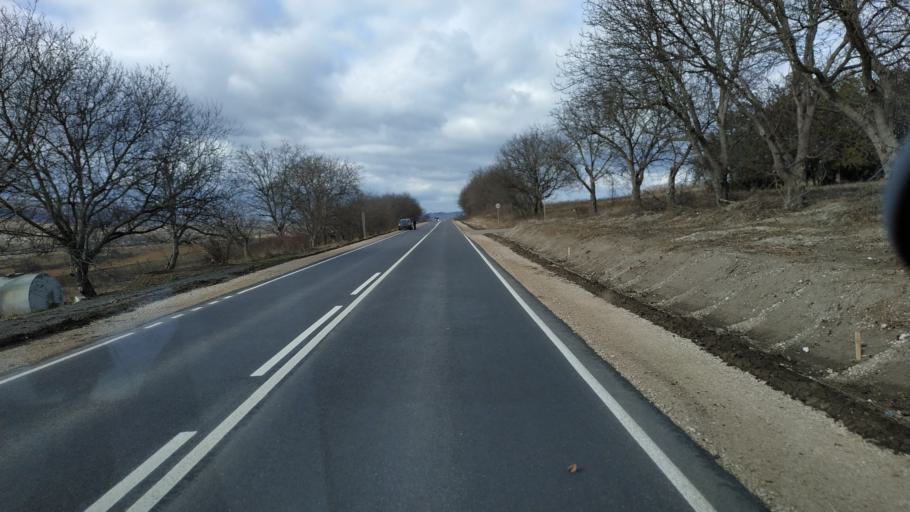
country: MD
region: Stinga Nistrului
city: Bucovat
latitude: 47.2066
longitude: 28.4213
